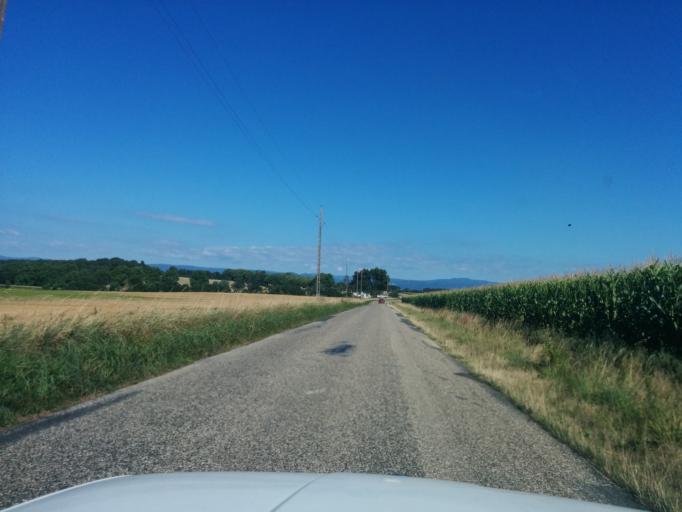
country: FR
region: Rhone-Alpes
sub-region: Departement de l'Ain
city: Perouges
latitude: 45.9518
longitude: 5.1655
